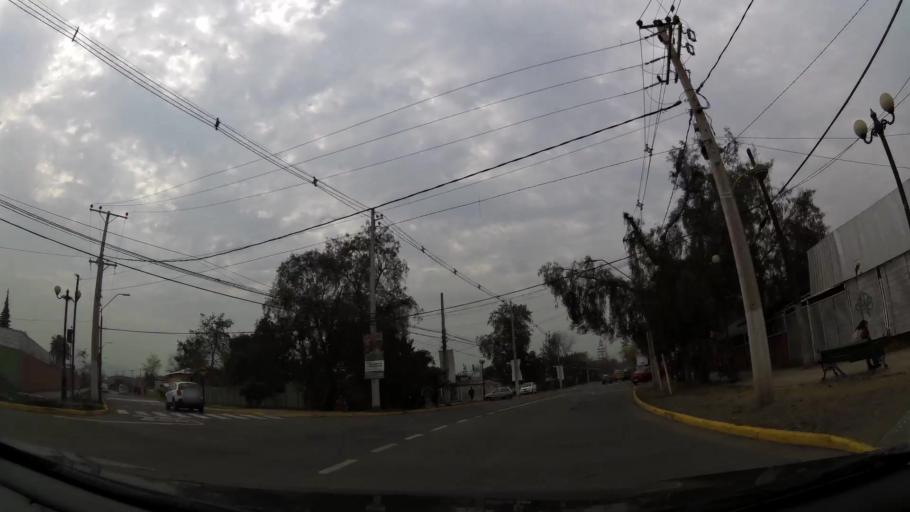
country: CL
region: Santiago Metropolitan
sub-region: Provincia de Chacabuco
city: Chicureo Abajo
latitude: -33.2040
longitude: -70.6825
